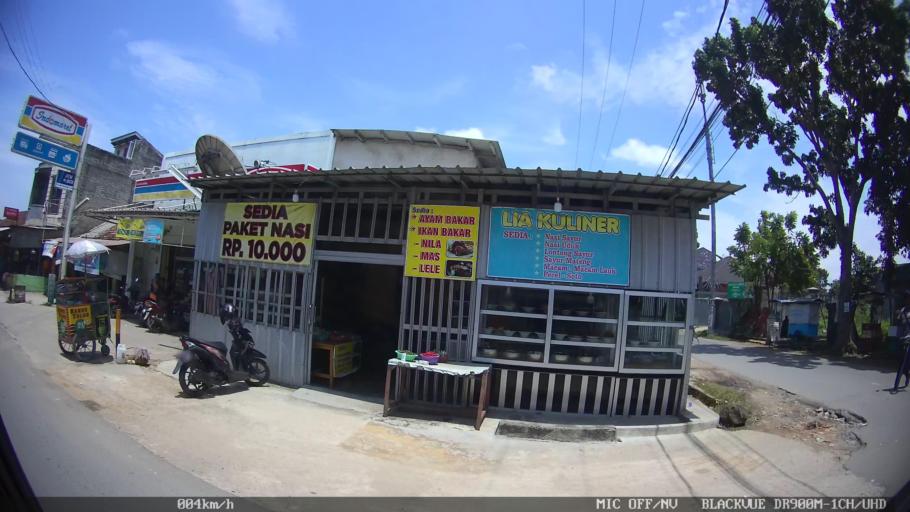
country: ID
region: Lampung
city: Kedaton
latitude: -5.3639
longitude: 105.2895
